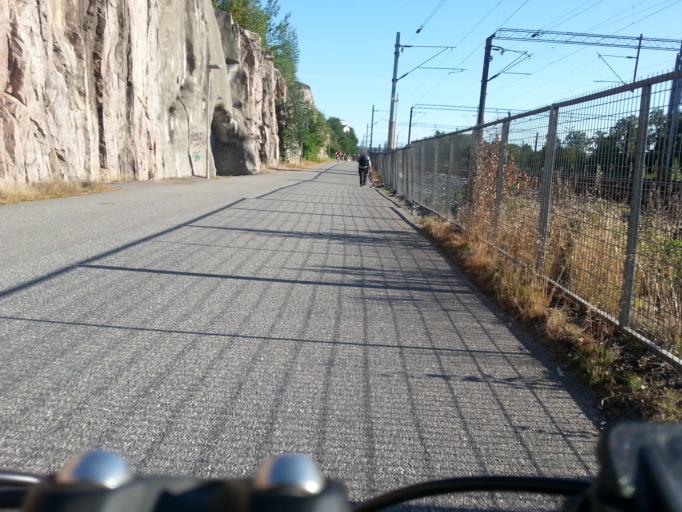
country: FI
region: Uusimaa
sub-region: Helsinki
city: Helsinki
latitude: 60.1874
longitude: 24.9361
